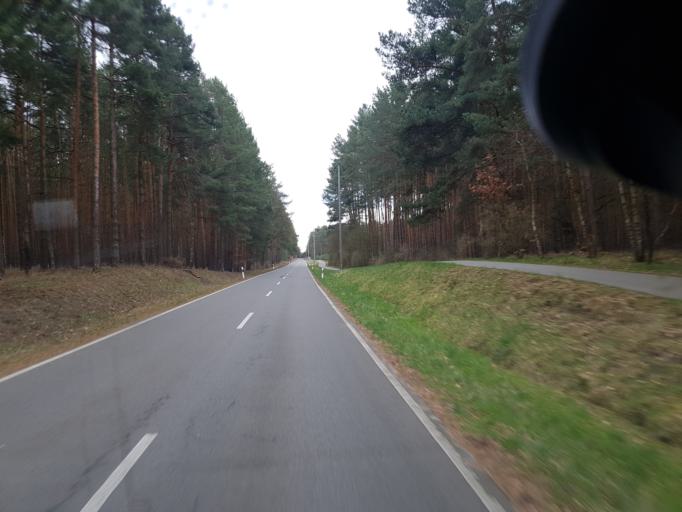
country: DE
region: Brandenburg
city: Mixdorf
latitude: 52.1901
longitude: 14.4230
